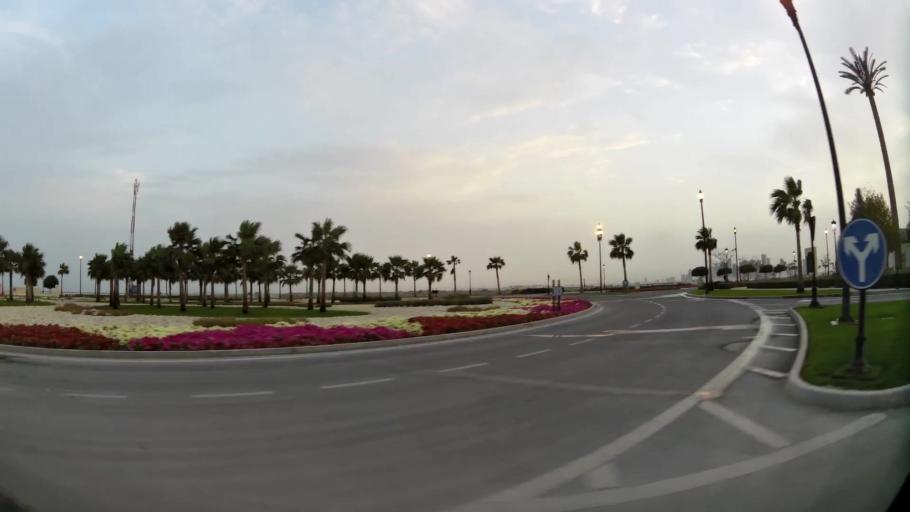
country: QA
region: Baladiyat ad Dawhah
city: Doha
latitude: 25.3593
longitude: 51.5693
